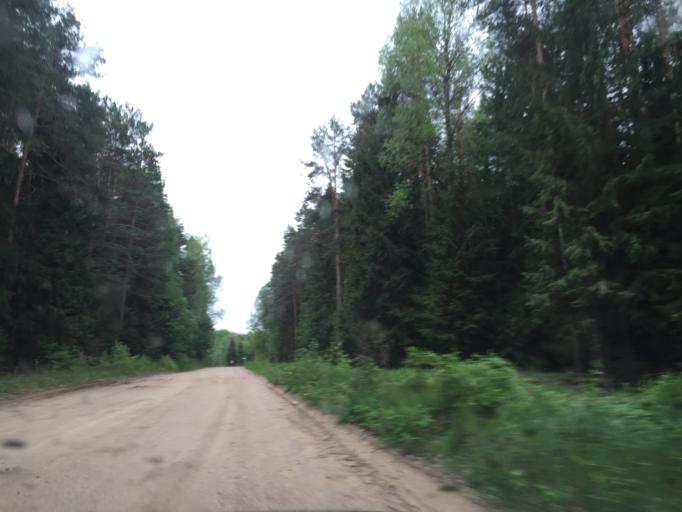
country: LV
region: Ogre
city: Ogre
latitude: 56.8270
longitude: 24.6492
